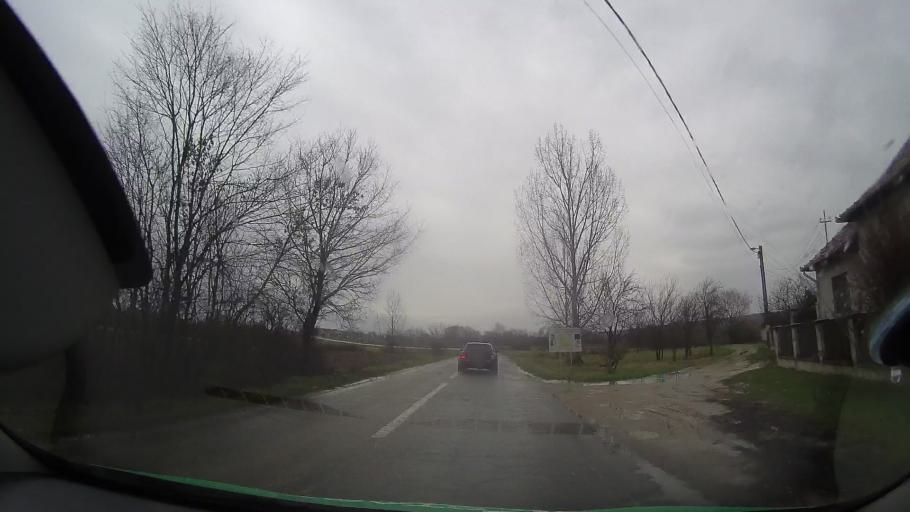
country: RO
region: Bihor
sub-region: Comuna Cociuba Mare
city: Cociuba Mare
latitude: 46.7400
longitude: 21.9865
